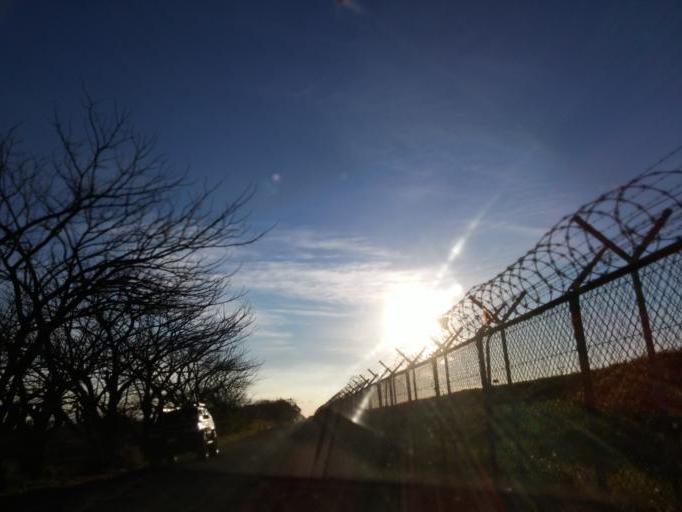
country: CR
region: Alajuela
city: Alajuela
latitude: 9.9946
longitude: -84.2040
